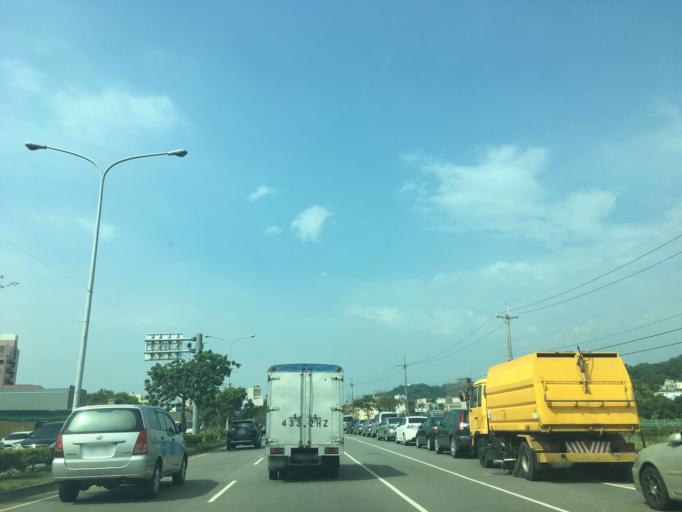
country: TW
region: Taiwan
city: Fengyuan
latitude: 24.2442
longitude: 120.7305
